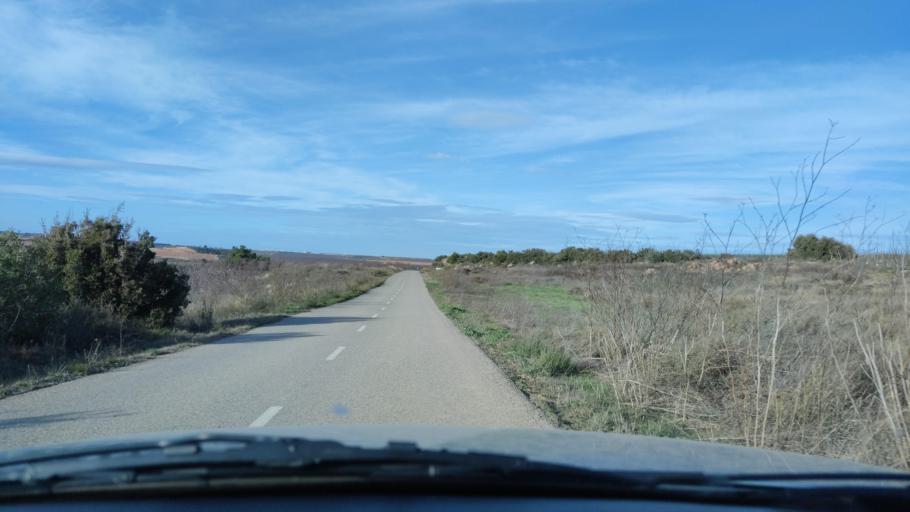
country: ES
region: Catalonia
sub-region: Provincia de Lleida
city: Alcano
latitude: 41.4680
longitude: 0.6466
